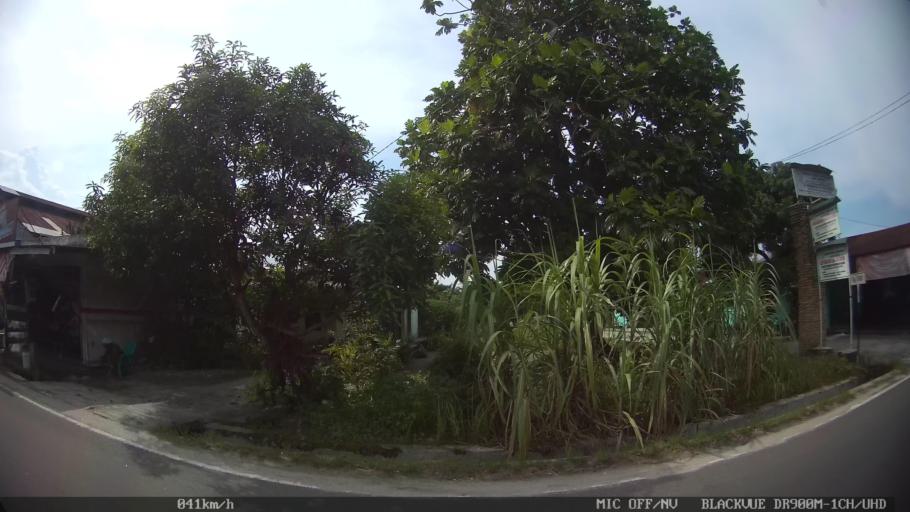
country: ID
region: North Sumatra
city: Percut
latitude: 3.6080
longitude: 98.7954
